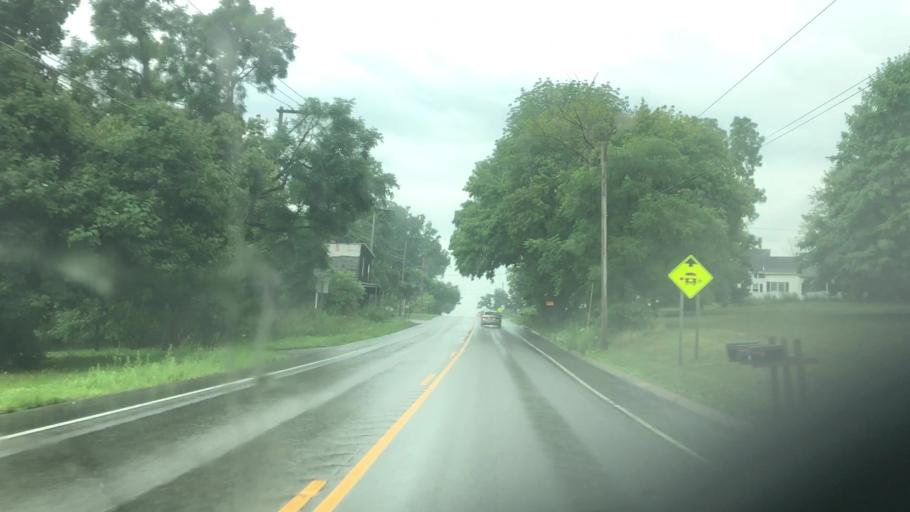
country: US
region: New York
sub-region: Monroe County
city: Fairport
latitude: 43.1290
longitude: -77.4144
